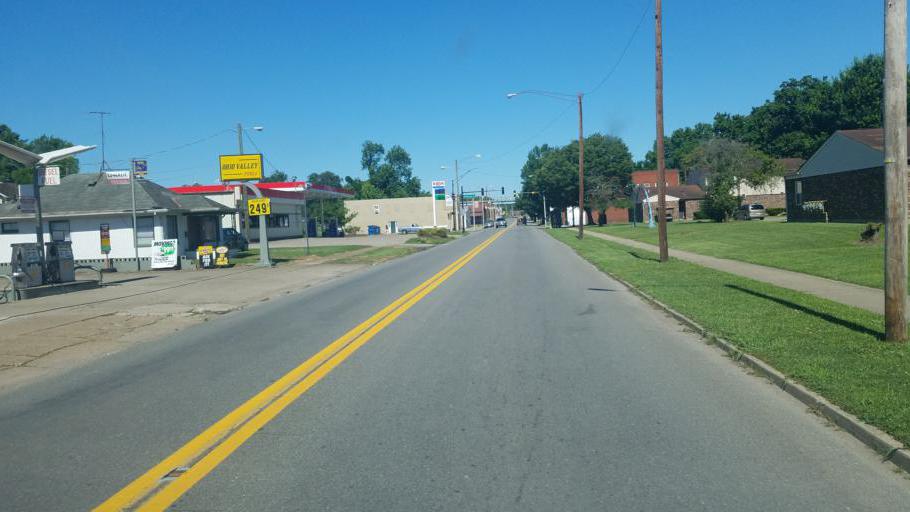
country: US
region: West Virginia
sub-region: Cabell County
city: Huntington
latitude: 38.4293
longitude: -82.3846
